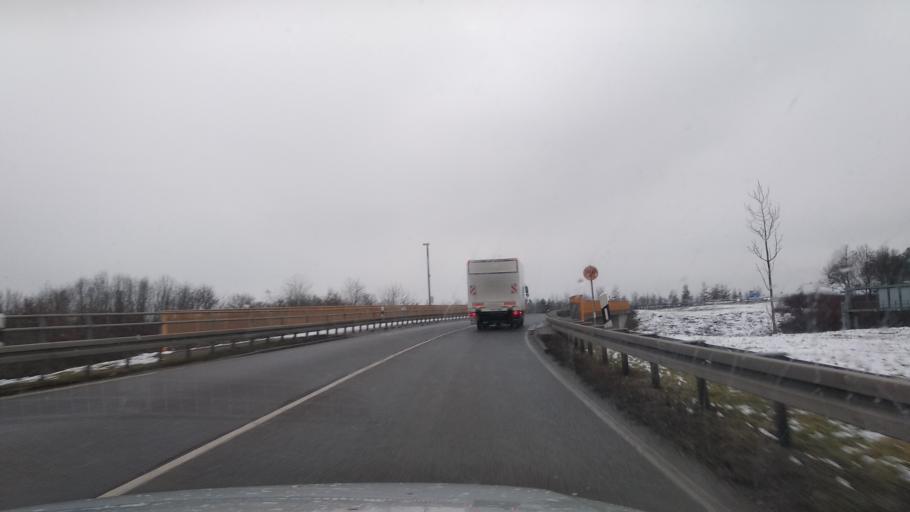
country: DE
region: Bavaria
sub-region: Upper Bavaria
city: Feldkirchen
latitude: 48.1437
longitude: 11.7450
